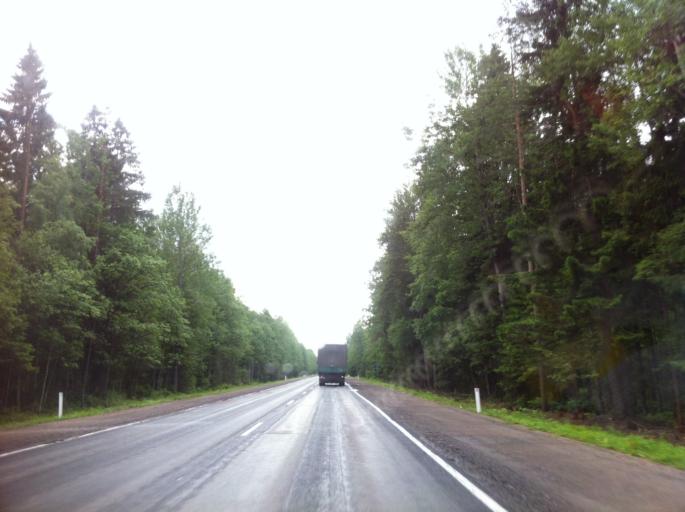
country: RU
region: Pskov
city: Strugi-Krasnyye
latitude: 58.1570
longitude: 29.2094
